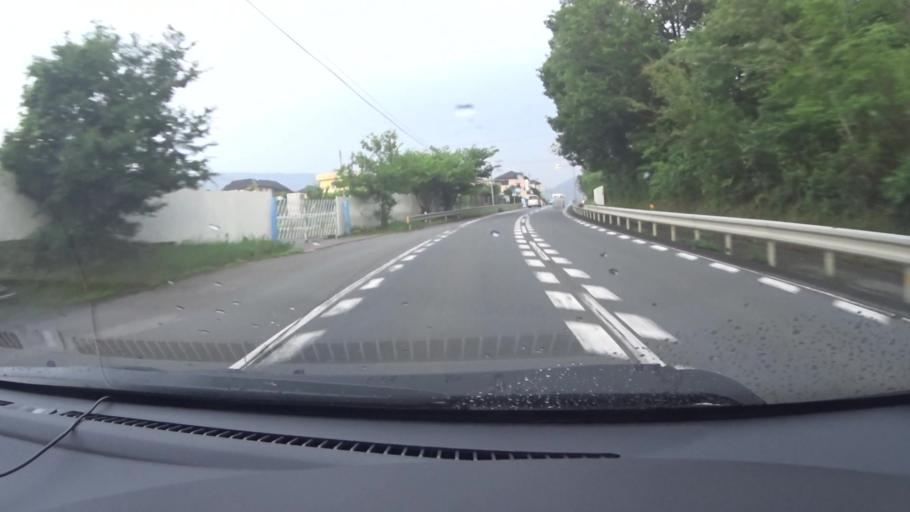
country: JP
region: Kyoto
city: Ayabe
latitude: 35.1730
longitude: 135.4245
